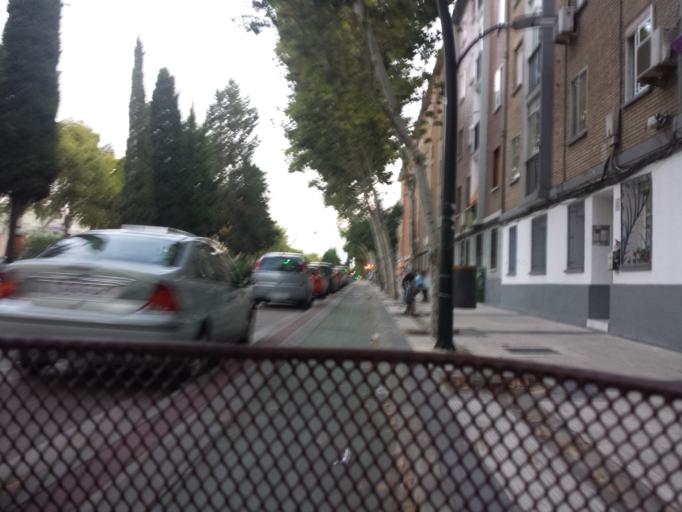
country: ES
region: Aragon
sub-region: Provincia de Zaragoza
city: Zaragoza
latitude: 41.6752
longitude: -0.8712
